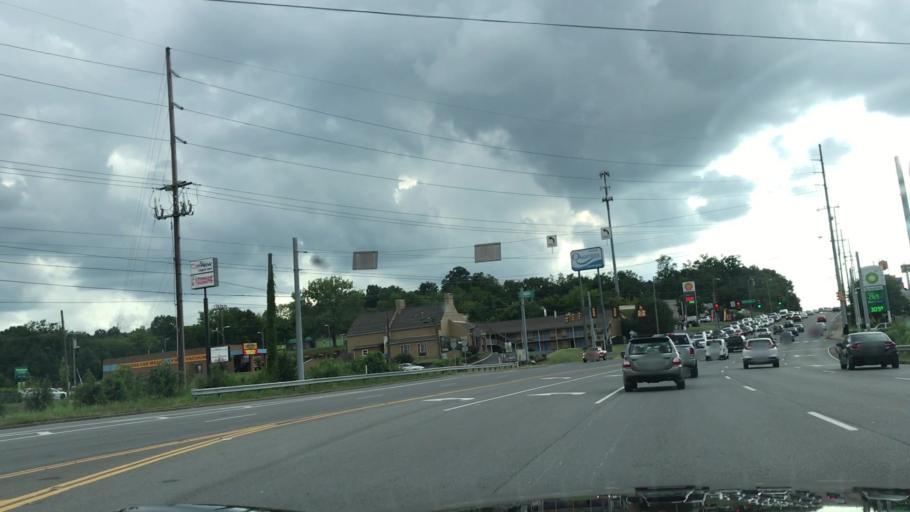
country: US
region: Tennessee
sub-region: Rutherford County
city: La Vergne
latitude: 36.0449
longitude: -86.6603
